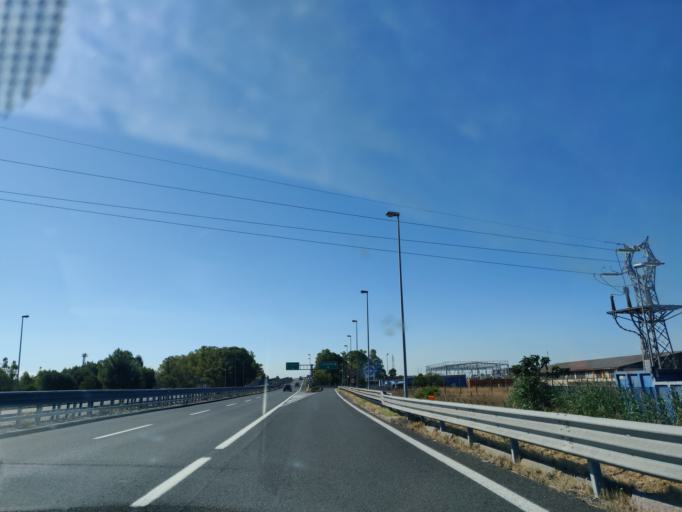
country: IT
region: Latium
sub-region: Citta metropolitana di Roma Capitale
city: Npp 23 (Parco Leonardo)
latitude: 41.8131
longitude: 12.3060
